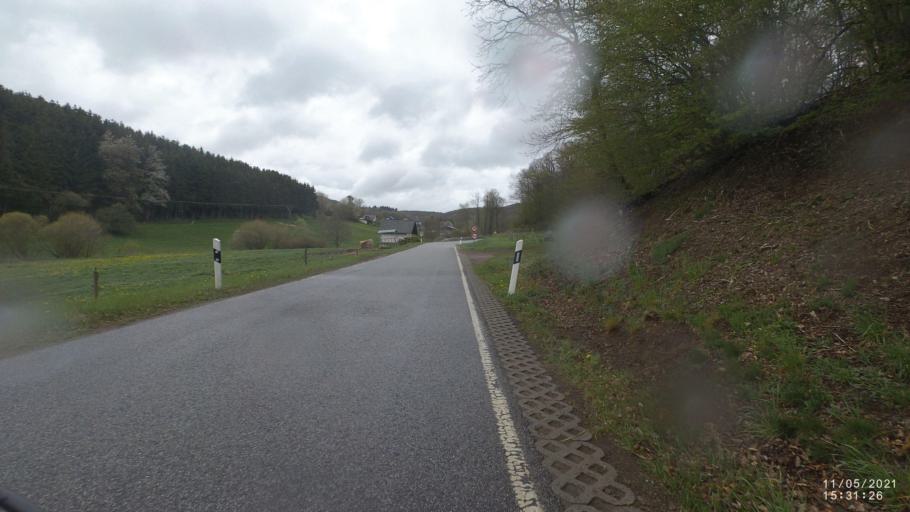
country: DE
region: Rheinland-Pfalz
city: Ditscheid
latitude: 50.3000
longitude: 7.0773
